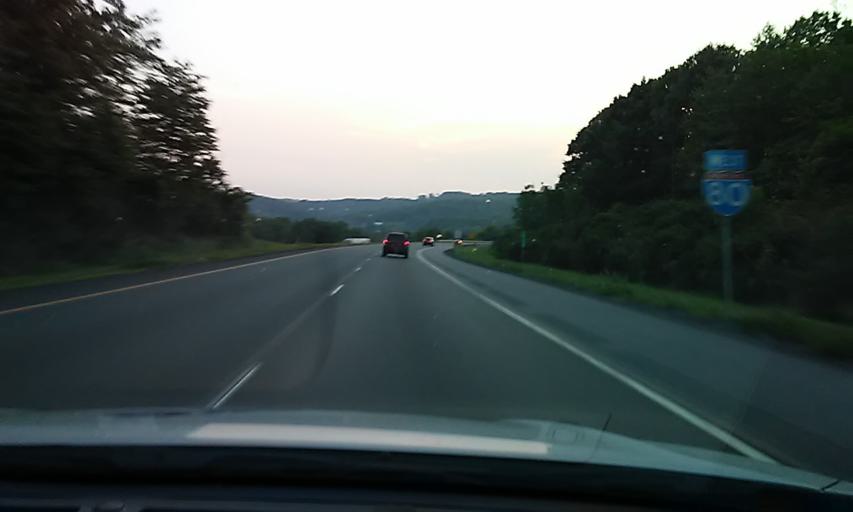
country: US
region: Pennsylvania
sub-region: Clarion County
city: Knox
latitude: 41.1849
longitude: -79.5494
